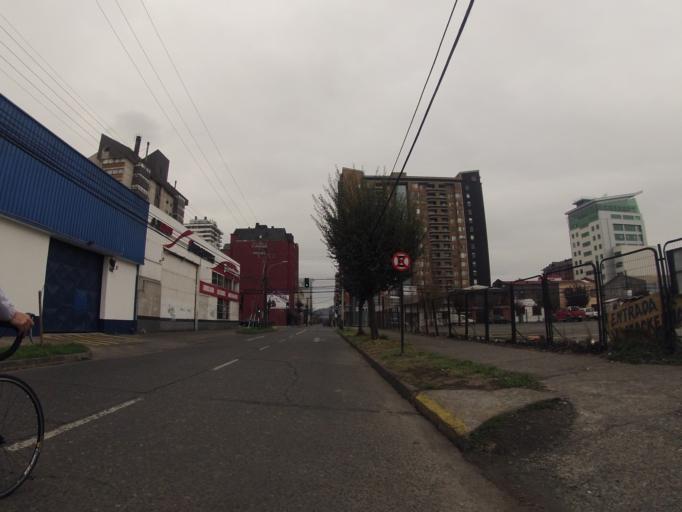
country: CL
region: Araucania
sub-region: Provincia de Cautin
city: Temuco
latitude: -38.7411
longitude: -72.5931
